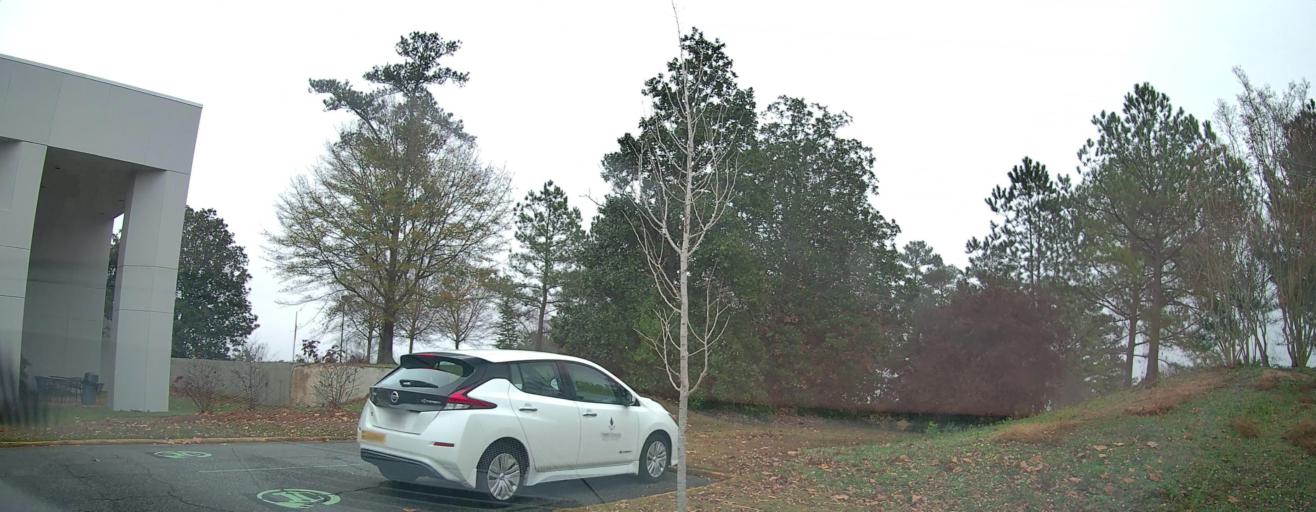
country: US
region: Georgia
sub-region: Bibb County
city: West Point
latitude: 32.8078
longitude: -83.7319
